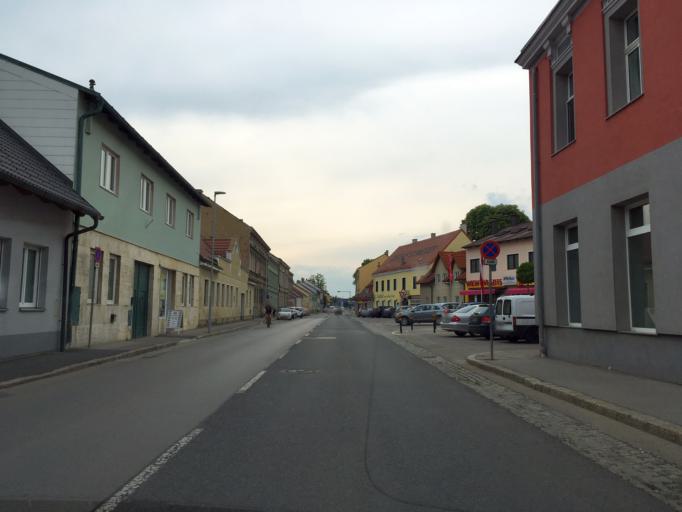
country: AT
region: Lower Austria
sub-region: Politischer Bezirk Korneuburg
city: Stockerau
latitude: 48.3848
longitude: 16.2034
